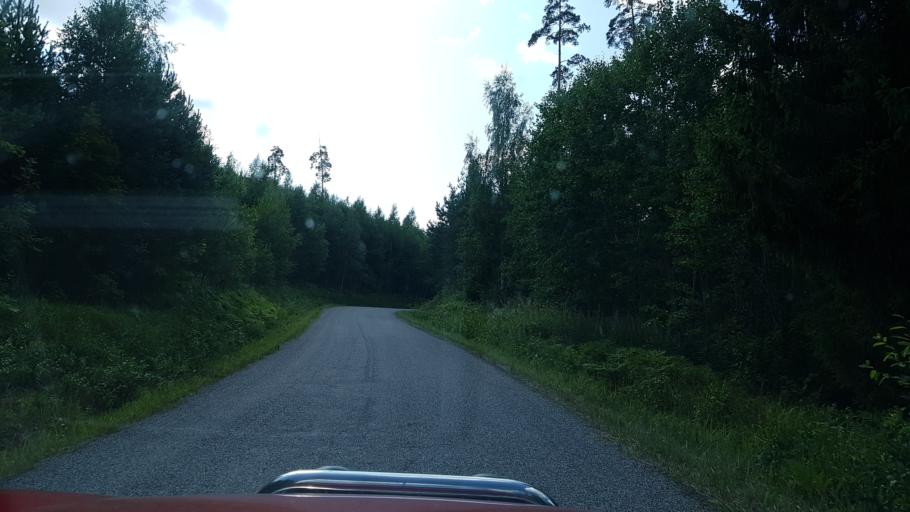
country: EE
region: Vorumaa
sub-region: Voru linn
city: Voru
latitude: 57.7180
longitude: 27.1993
